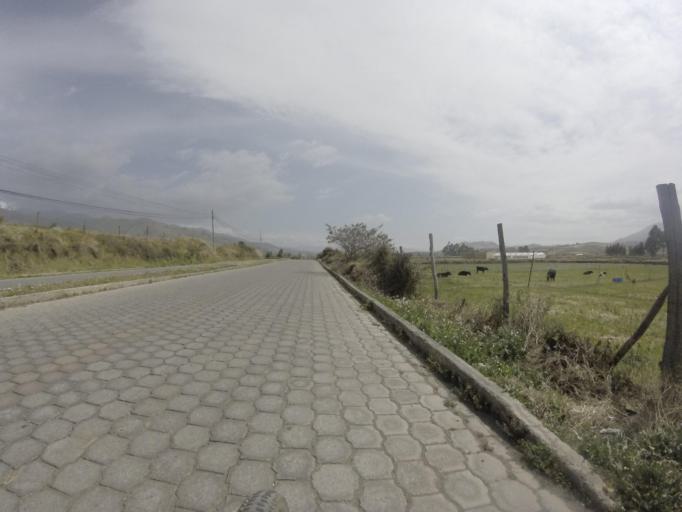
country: EC
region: Pichincha
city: Cayambe
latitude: 0.1429
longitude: -78.0718
